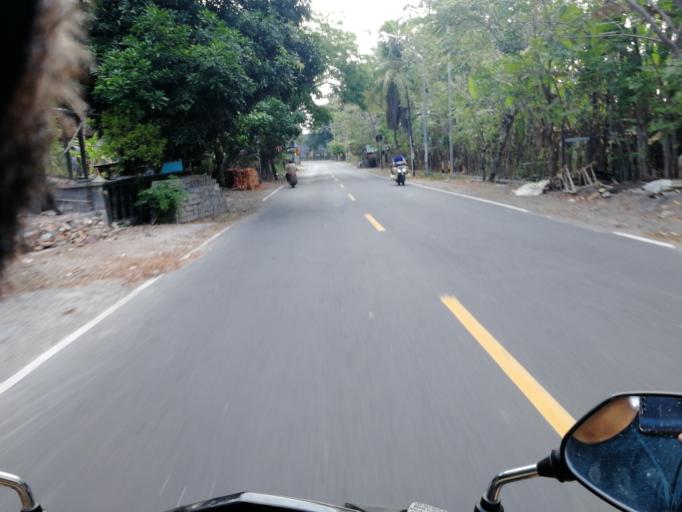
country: ID
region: West Nusa Tenggara
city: Karangsubagan
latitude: -8.4903
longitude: 116.0411
